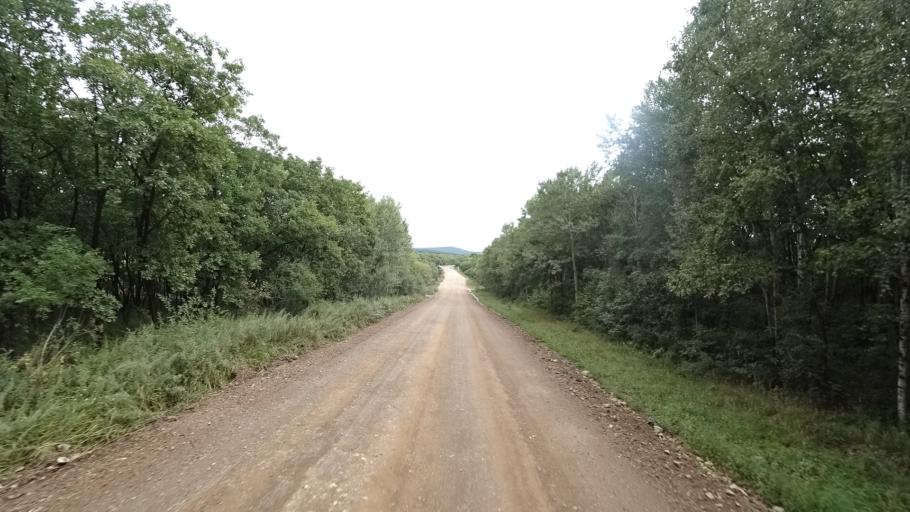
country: RU
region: Primorskiy
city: Lyalichi
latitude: 44.0838
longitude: 132.4448
